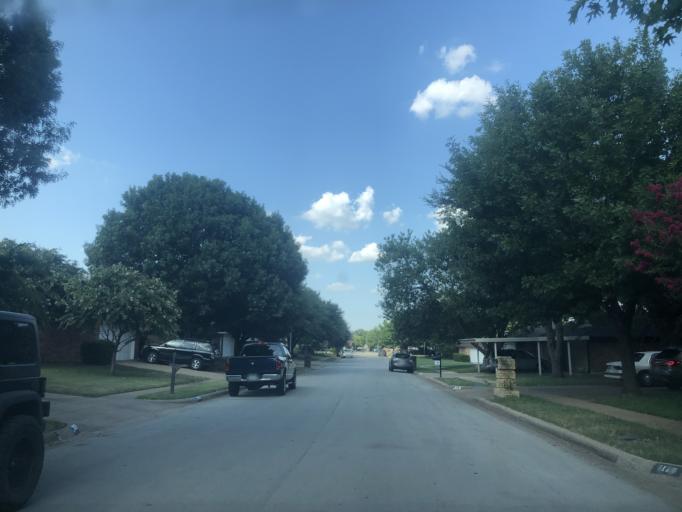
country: US
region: Texas
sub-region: Tarrant County
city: Saginaw
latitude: 32.8519
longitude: -97.3865
